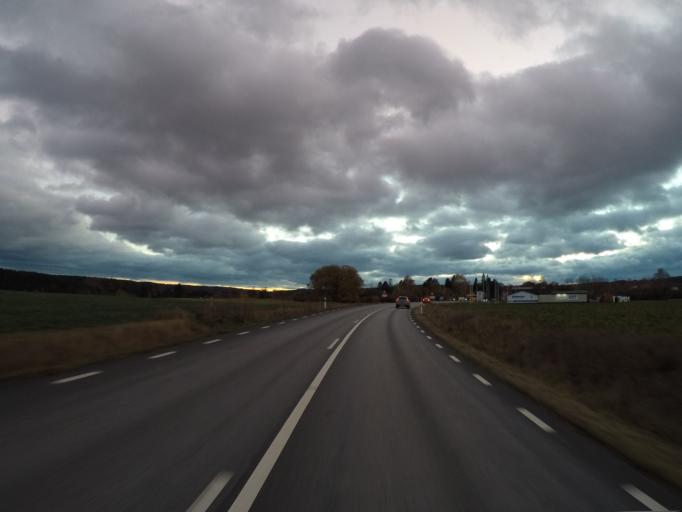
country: SE
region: Skane
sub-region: Kristianstads Kommun
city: Degeberga
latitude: 55.8435
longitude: 14.0953
